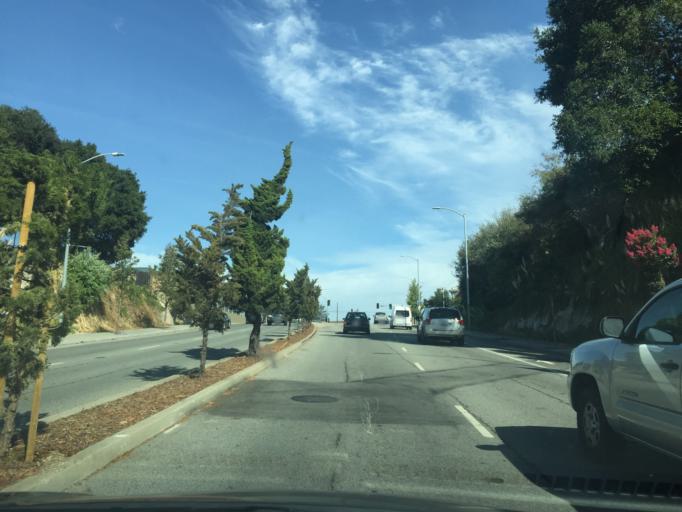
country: US
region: California
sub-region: Santa Cruz County
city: Santa Cruz
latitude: 36.9811
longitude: -122.0159
